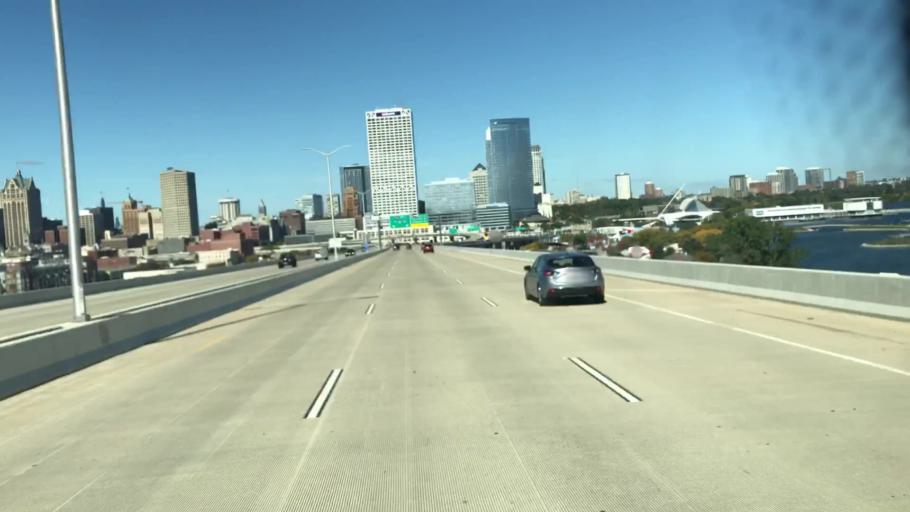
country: US
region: Wisconsin
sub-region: Milwaukee County
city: Milwaukee
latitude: 43.0273
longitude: -87.8993
